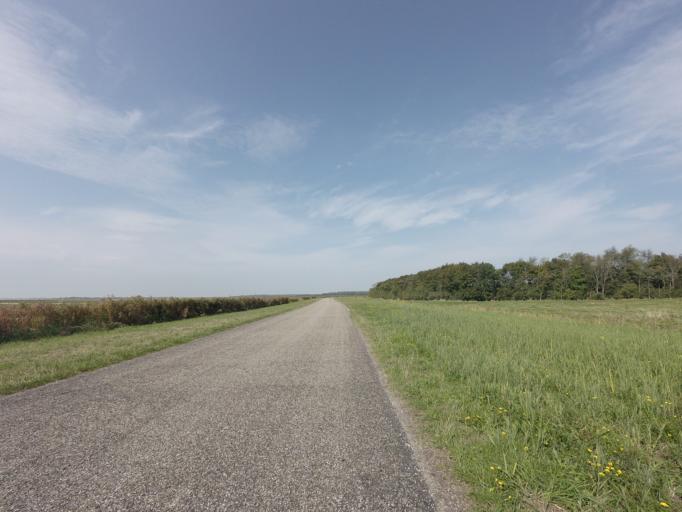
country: NL
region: Groningen
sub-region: Gemeente De Marne
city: Ulrum
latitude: 53.3561
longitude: 6.2637
